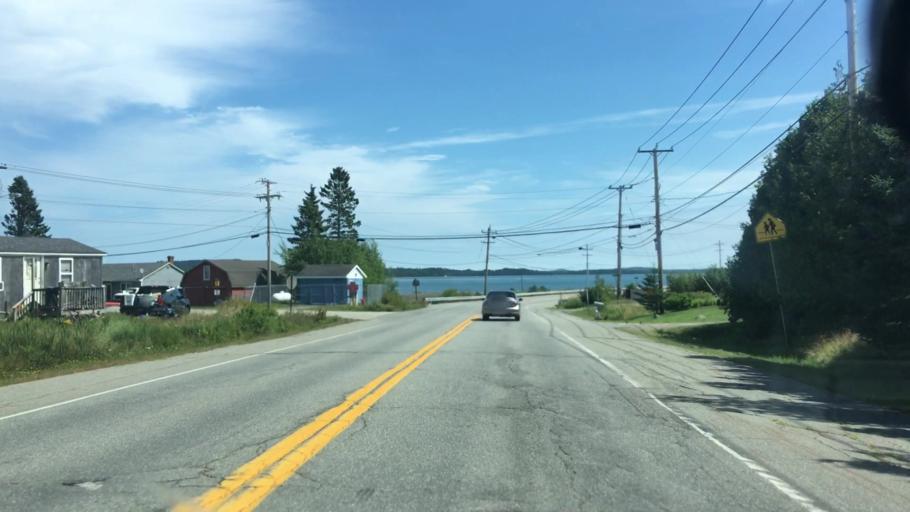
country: US
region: Maine
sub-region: Washington County
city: Eastport
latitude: 44.9552
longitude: -67.0421
